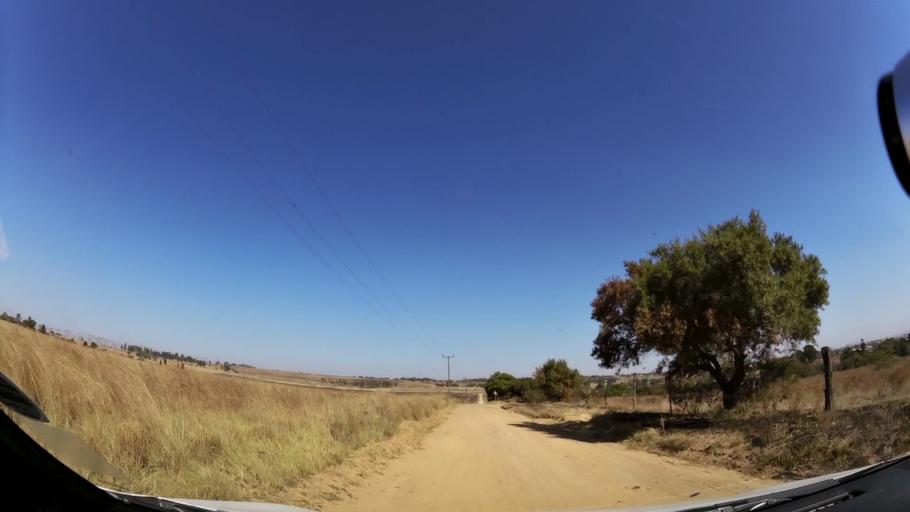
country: ZA
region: Gauteng
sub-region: City of Johannesburg Metropolitan Municipality
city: Diepsloot
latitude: -25.9014
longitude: 28.0737
